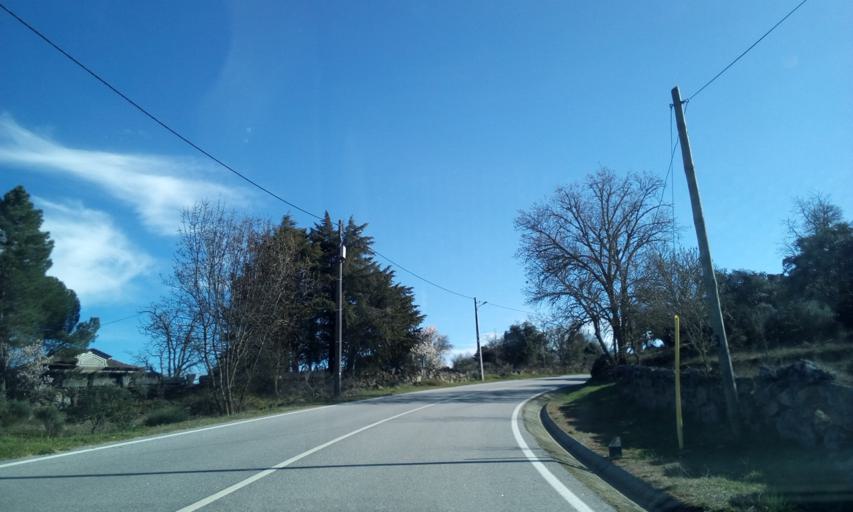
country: ES
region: Castille and Leon
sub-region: Provincia de Salamanca
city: Fuentes de Onoro
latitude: 40.6175
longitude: -6.8922
